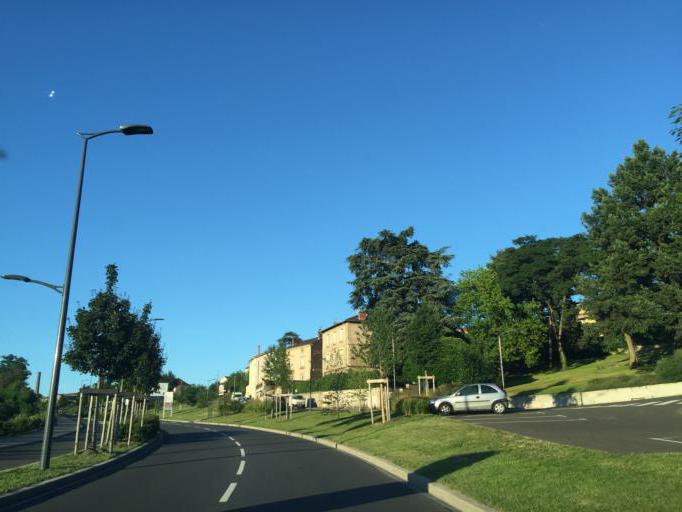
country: FR
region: Rhone-Alpes
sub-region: Departement de la Loire
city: Saint-Chamond
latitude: 45.4643
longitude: 4.4987
